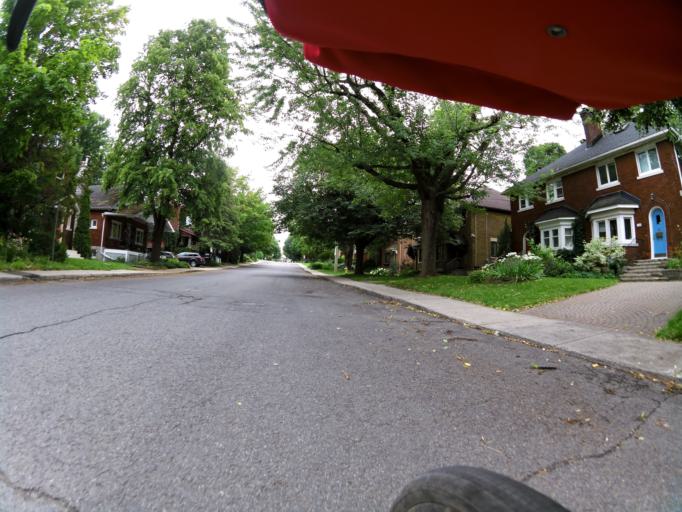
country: CA
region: Ontario
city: Ottawa
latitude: 45.4239
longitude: -75.6739
